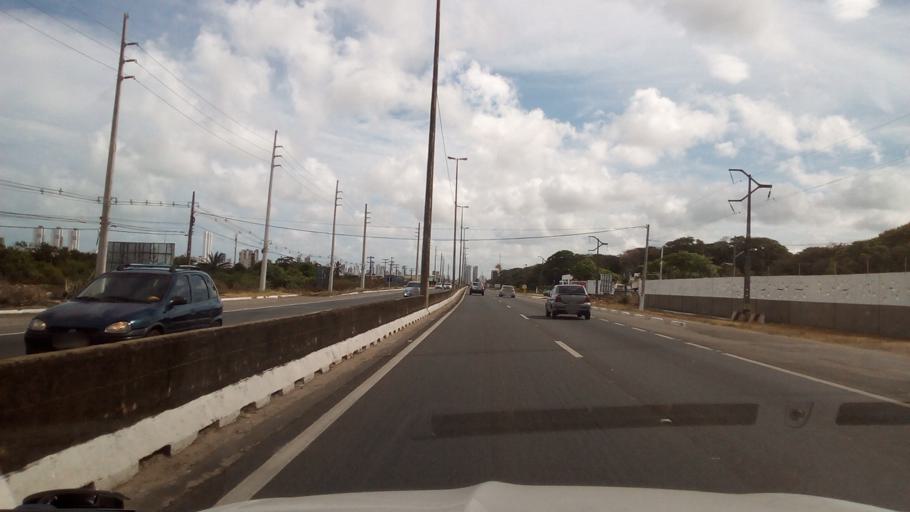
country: BR
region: Paraiba
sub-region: Joao Pessoa
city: Joao Pessoa
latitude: -7.0576
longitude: -34.8507
